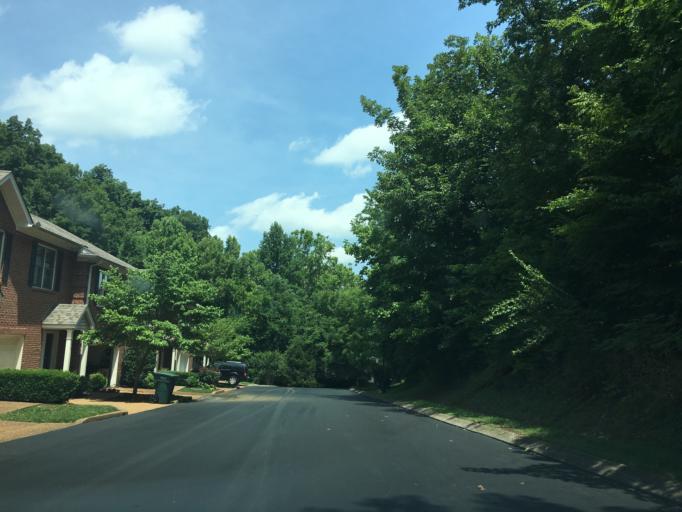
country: US
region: Tennessee
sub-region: Davidson County
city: Belle Meade
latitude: 36.0737
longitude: -86.9102
